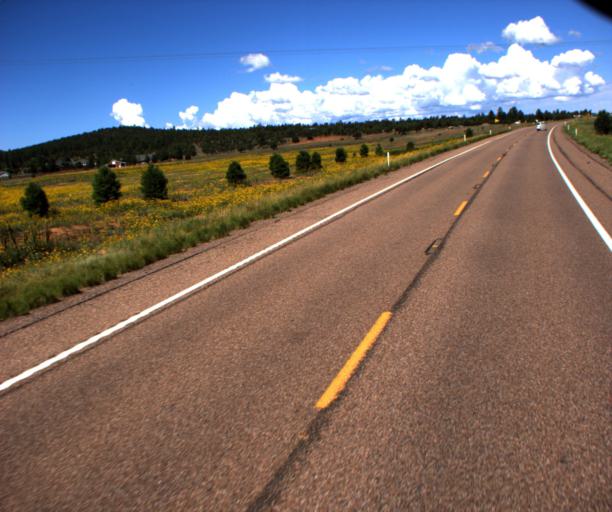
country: US
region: Arizona
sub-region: Navajo County
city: Linden
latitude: 34.3151
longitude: -110.2429
